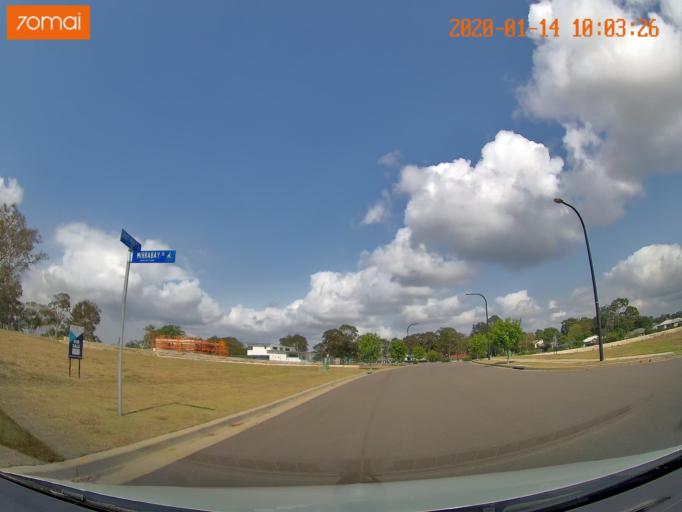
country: AU
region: New South Wales
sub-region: Wyong Shire
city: Kingfisher Shores
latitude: -33.1262
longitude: 151.5391
